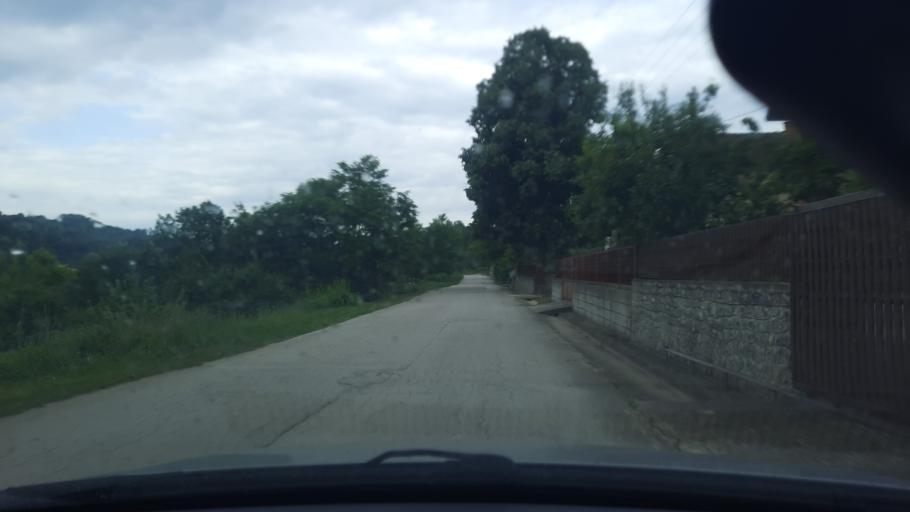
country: RS
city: Jarebice
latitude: 44.4832
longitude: 19.4802
